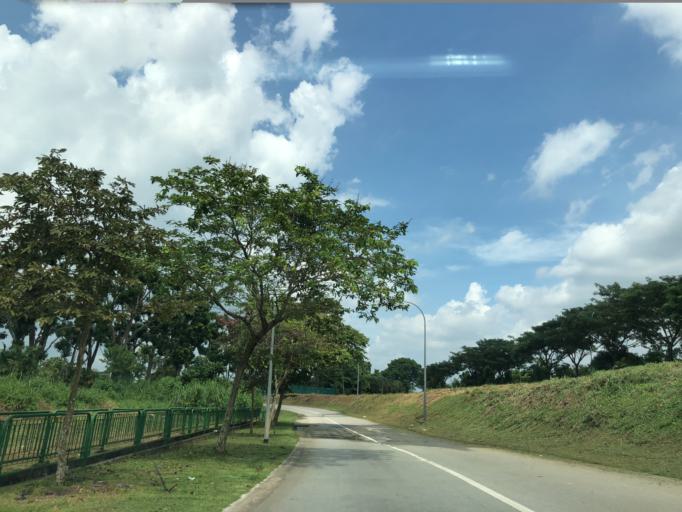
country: MY
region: Johor
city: Kampung Pasir Gudang Baru
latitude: 1.4128
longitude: 103.8615
